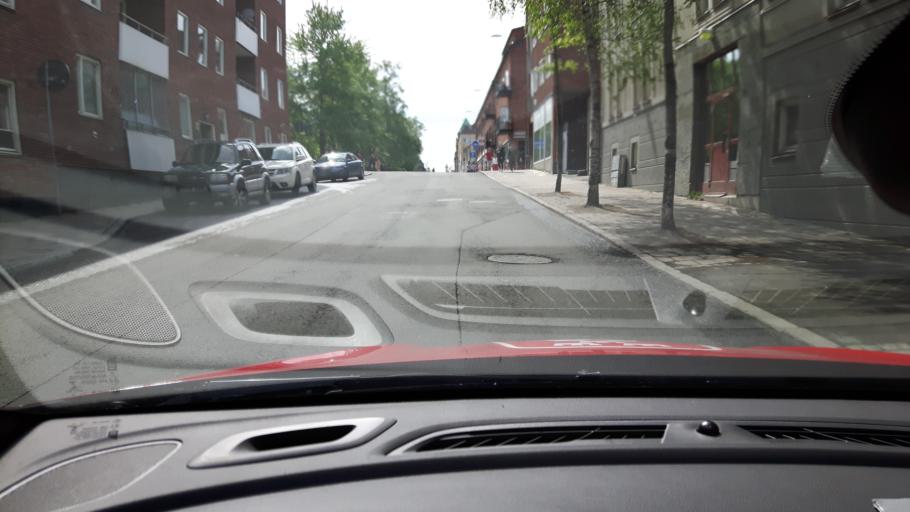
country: SE
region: Jaemtland
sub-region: OEstersunds Kommun
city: Ostersund
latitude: 63.1798
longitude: 14.6383
